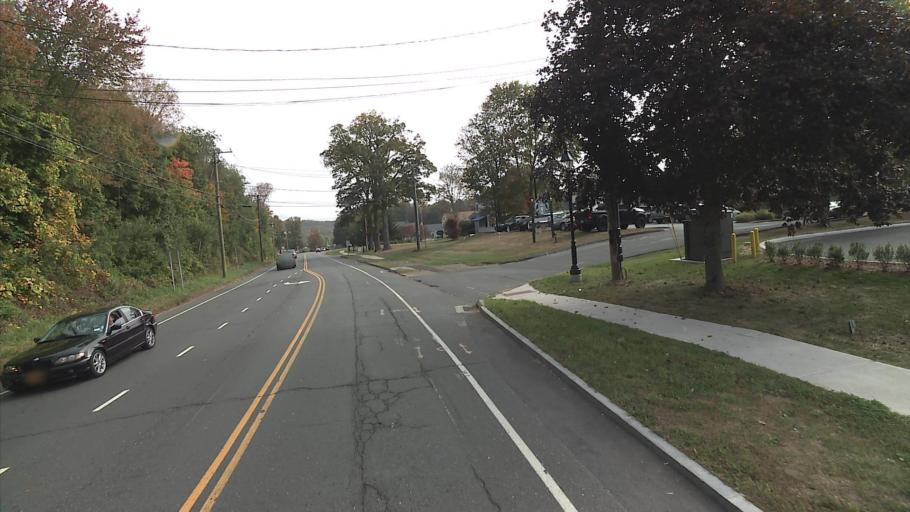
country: US
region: Connecticut
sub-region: Fairfield County
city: Newtown
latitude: 41.4151
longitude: -73.3002
